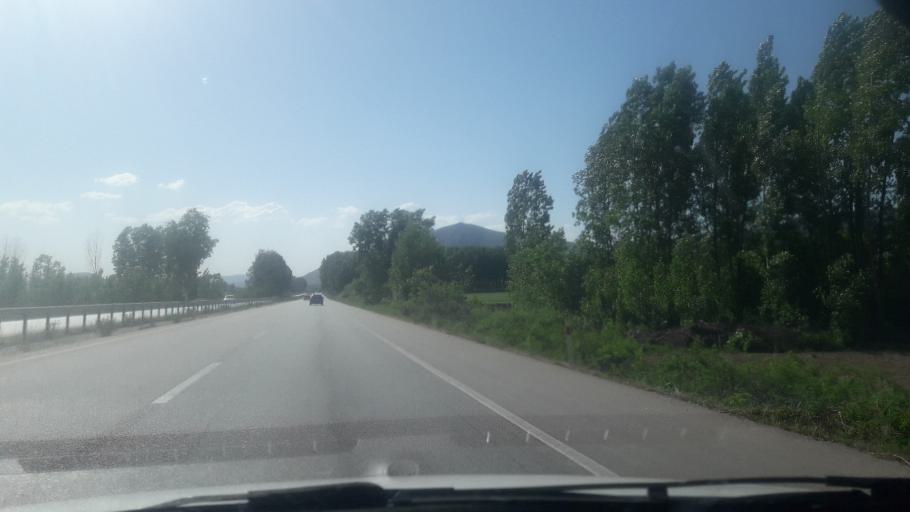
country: TR
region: Tokat
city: Dokmetepe
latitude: 40.3167
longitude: 36.2480
